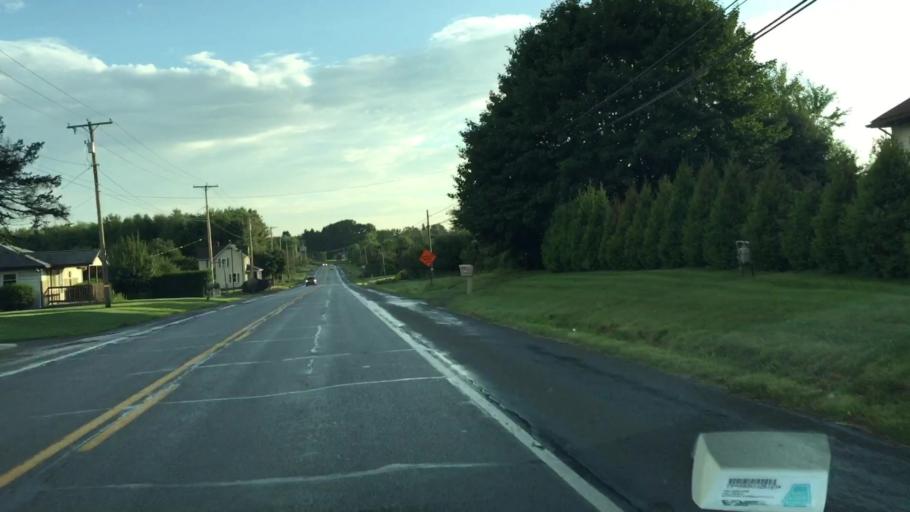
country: US
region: Pennsylvania
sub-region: Butler County
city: Meridian
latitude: 40.8402
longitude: -79.9972
